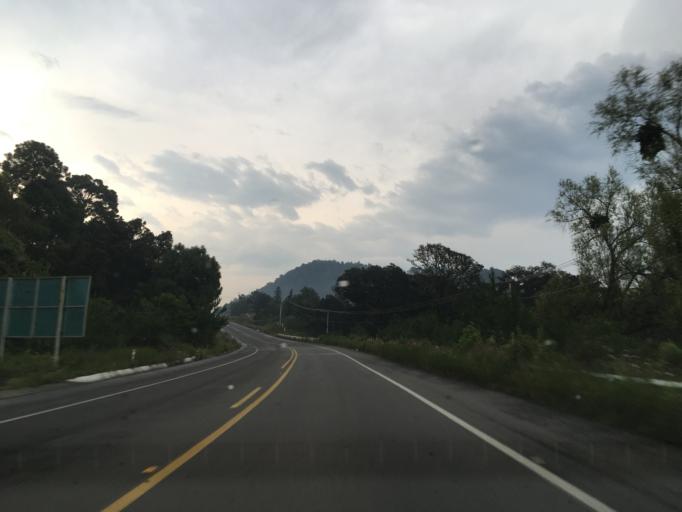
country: MX
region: Michoacan
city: Capacuaro
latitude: 19.5102
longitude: -102.1187
